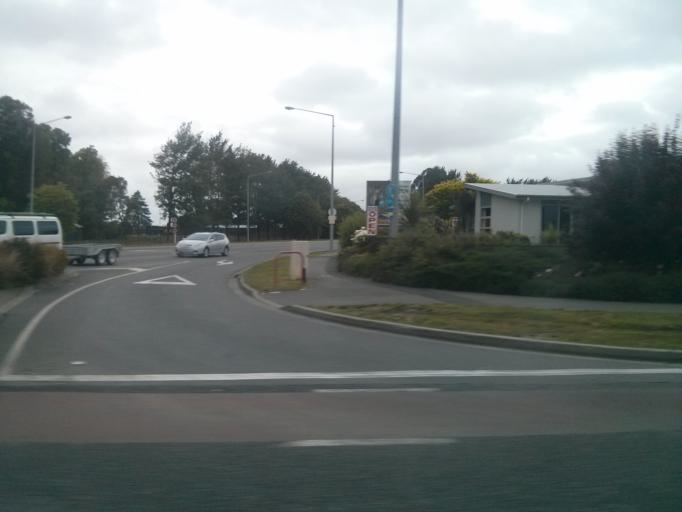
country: NZ
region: Canterbury
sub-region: Christchurch City
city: Christchurch
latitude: -43.4848
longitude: 172.6164
